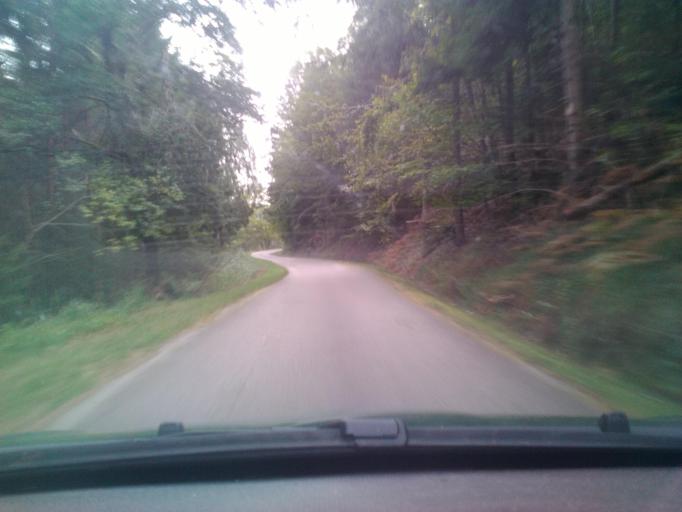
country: FR
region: Lorraine
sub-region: Departement des Vosges
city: Corcieux
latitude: 48.2060
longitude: 6.8798
